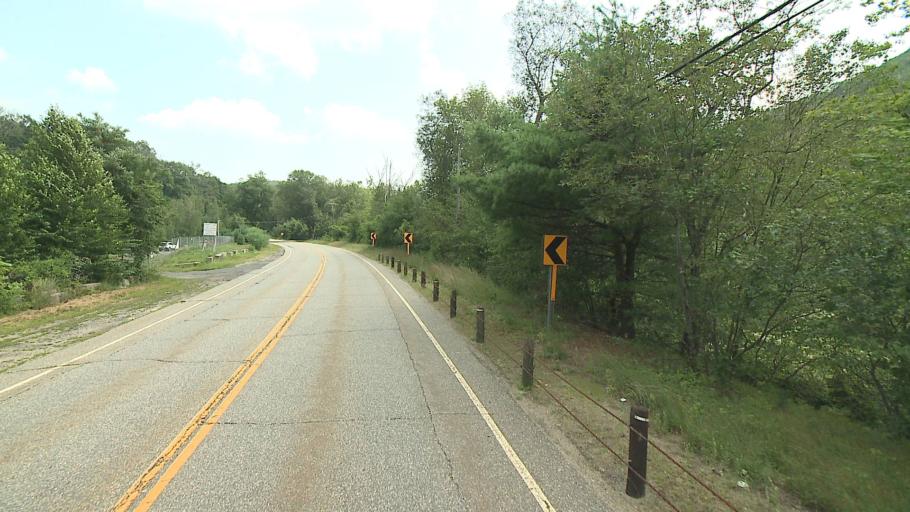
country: US
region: Connecticut
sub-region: Litchfield County
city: Oakville
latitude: 41.6229
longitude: -73.0655
